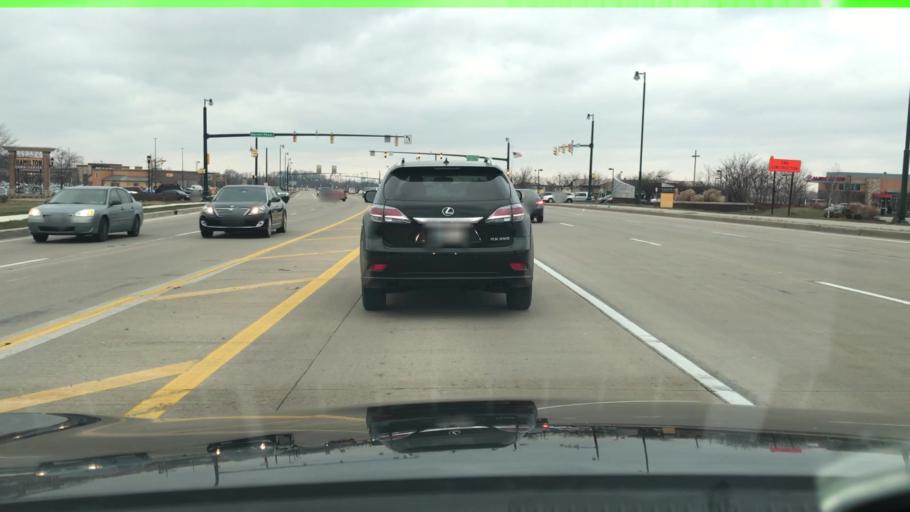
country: US
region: Indiana
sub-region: Hancock County
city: McCordsville
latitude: 39.9933
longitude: -85.9274
